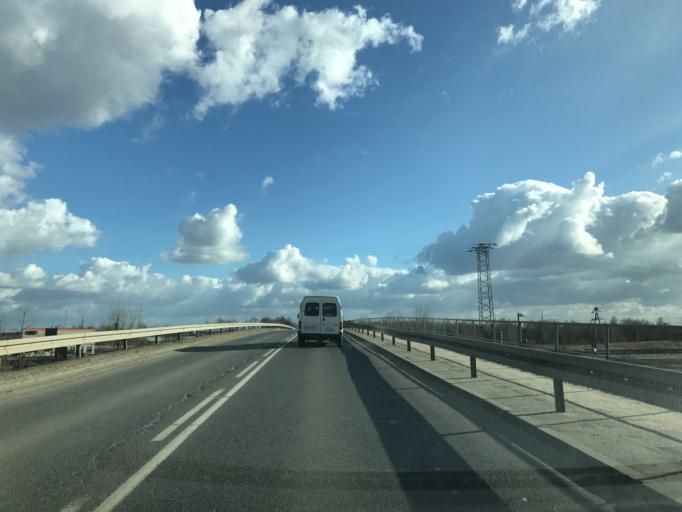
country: PL
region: Masovian Voivodeship
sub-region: Powiat wolominski
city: Radzymin
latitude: 52.4038
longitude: 21.1937
